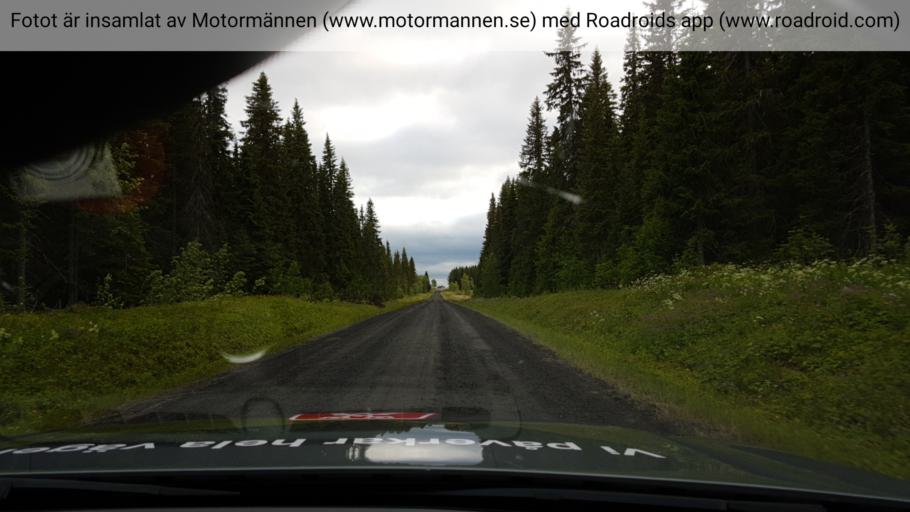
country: SE
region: Jaemtland
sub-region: OEstersunds Kommun
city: Lit
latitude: 63.6195
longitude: 15.0124
